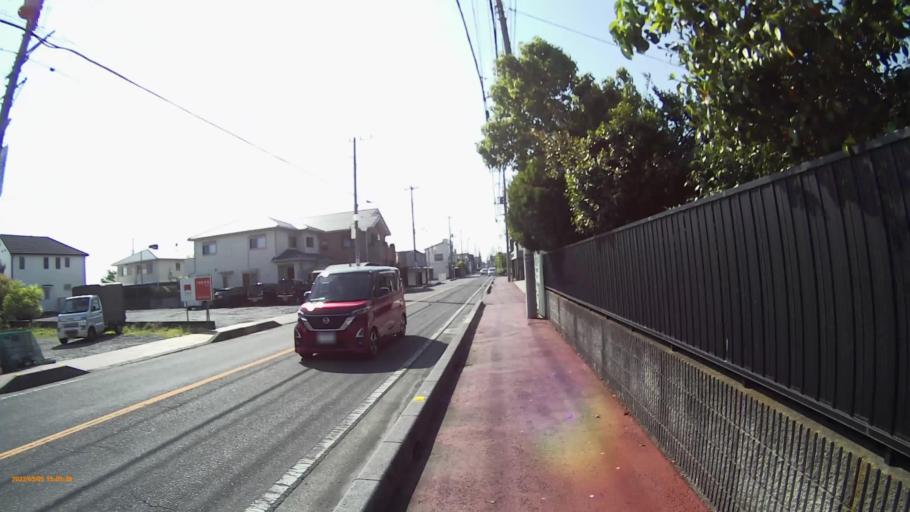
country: JP
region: Saitama
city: Sugito
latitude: 36.0263
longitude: 139.7342
